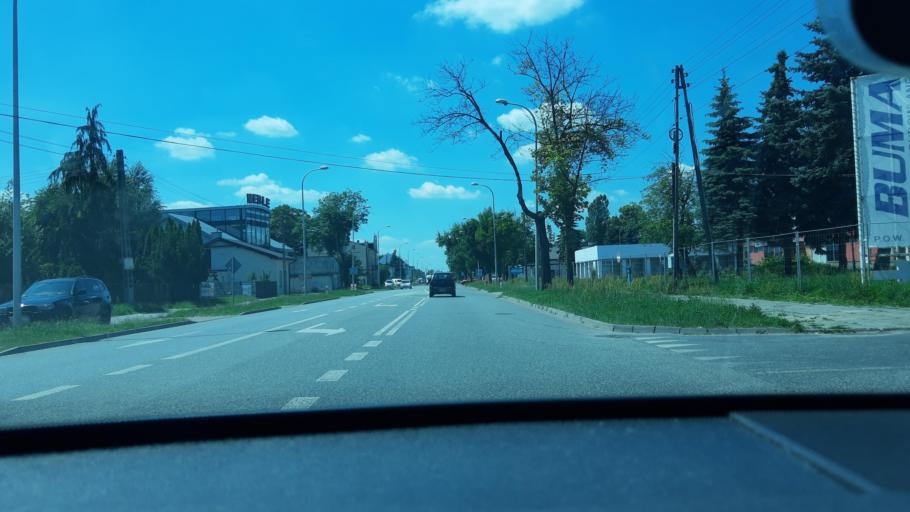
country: PL
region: Lodz Voivodeship
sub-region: Powiat sieradzki
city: Sieradz
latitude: 51.5955
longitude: 18.7214
